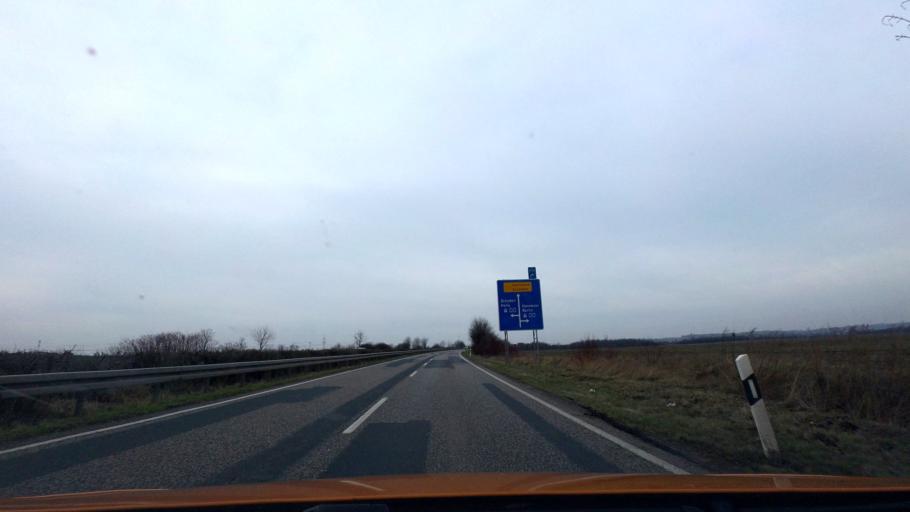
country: DE
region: Saxony-Anhalt
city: Diesdorf
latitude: 52.1416
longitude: 11.5516
